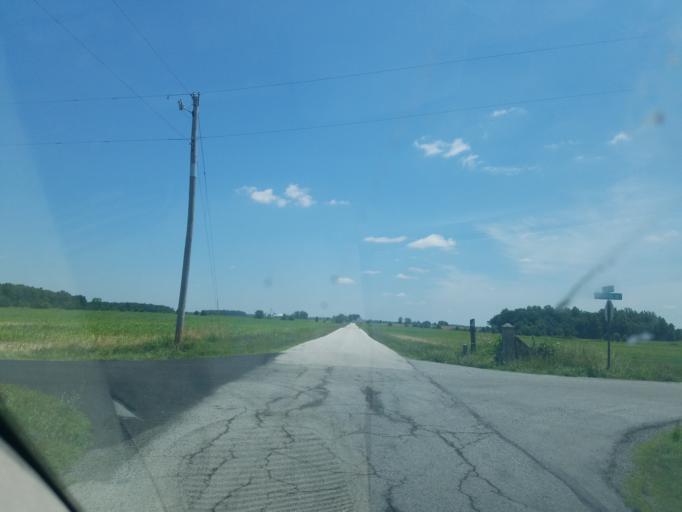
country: US
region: Ohio
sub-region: Hancock County
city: Arlington
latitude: 40.8483
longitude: -83.6143
